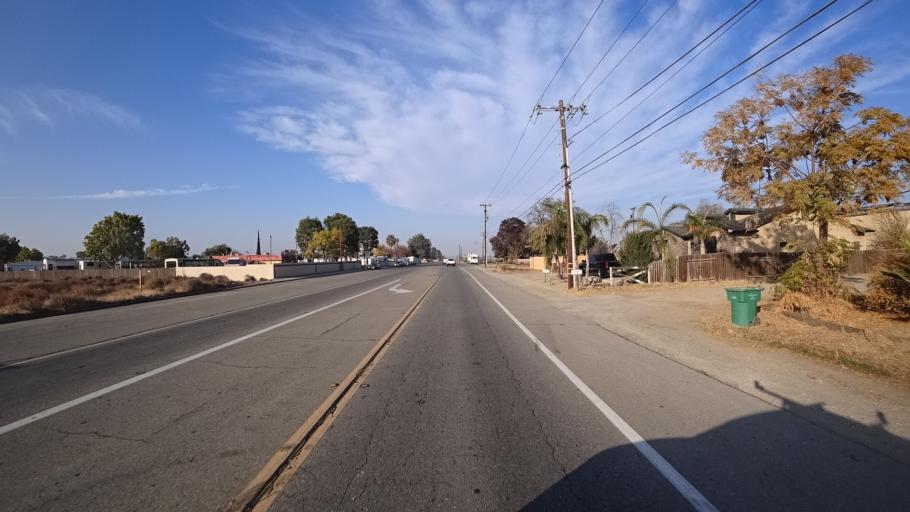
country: US
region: California
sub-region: Kern County
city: Rosedale
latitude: 35.3837
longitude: -119.1557
